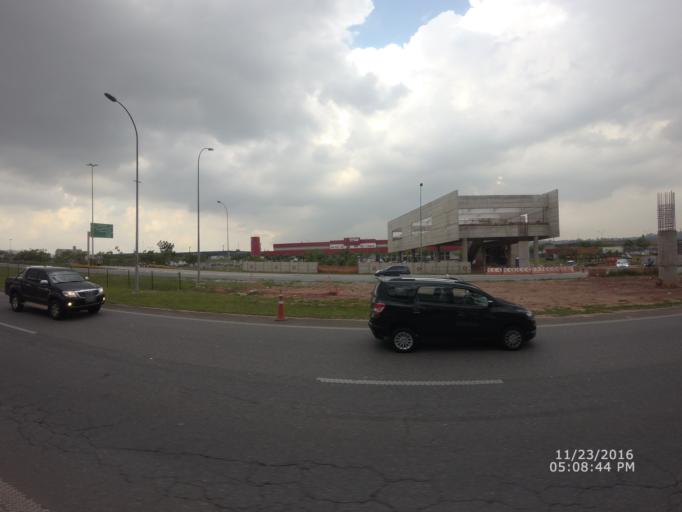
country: BR
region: Sao Paulo
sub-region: Guarulhos
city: Guarulhos
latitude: -23.4324
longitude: -46.4934
